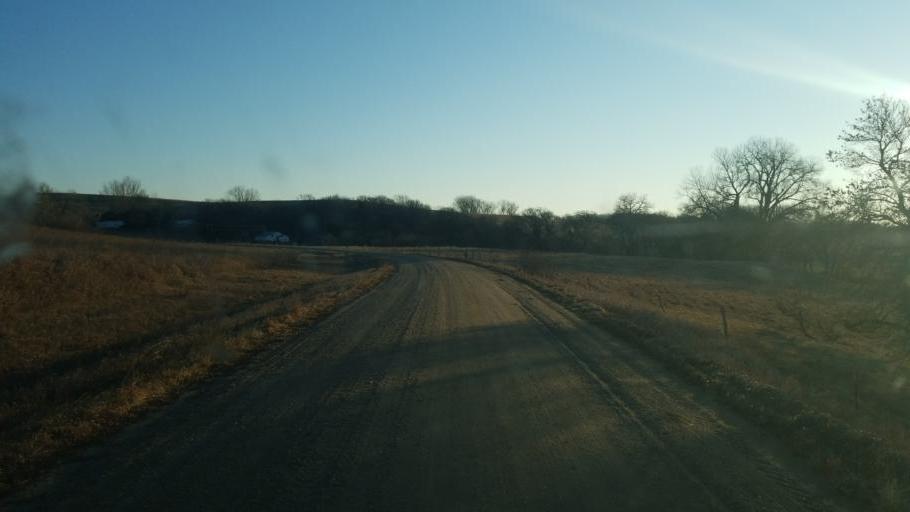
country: US
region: Nebraska
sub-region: Knox County
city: Center
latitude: 42.5580
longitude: -97.7978
